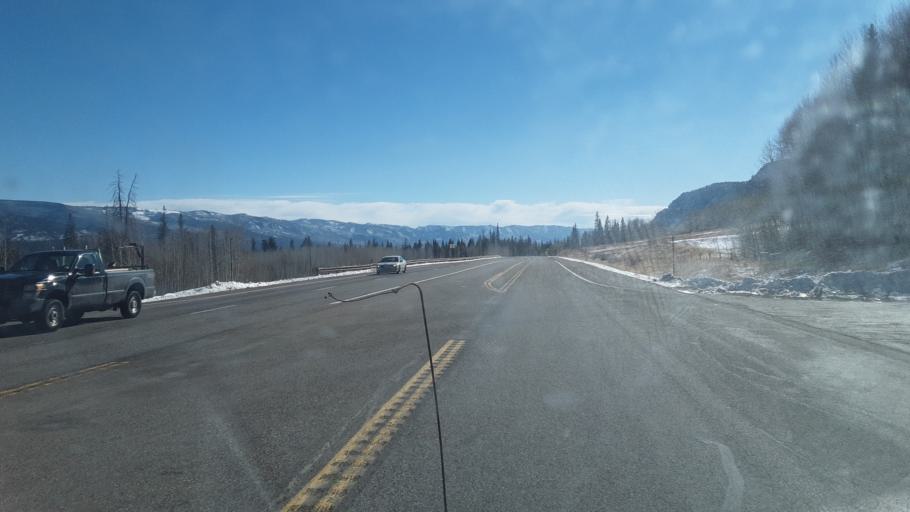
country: US
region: Colorado
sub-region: San Juan County
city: Silverton
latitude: 37.5821
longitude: -107.8235
